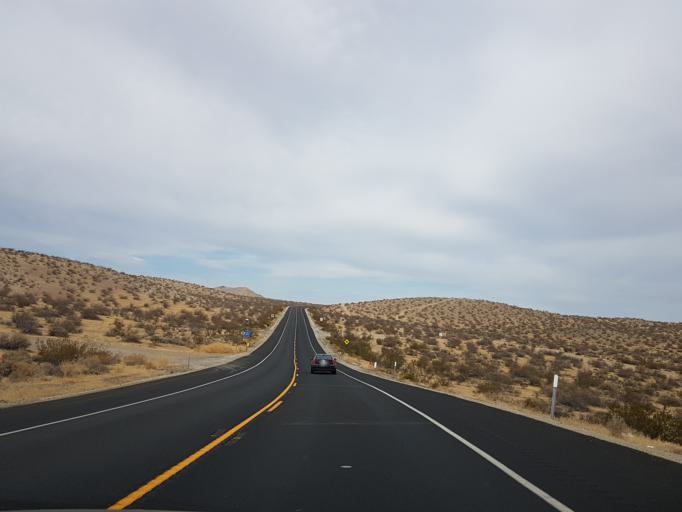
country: US
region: California
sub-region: Kern County
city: Ridgecrest
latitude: 35.4544
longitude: -117.6544
